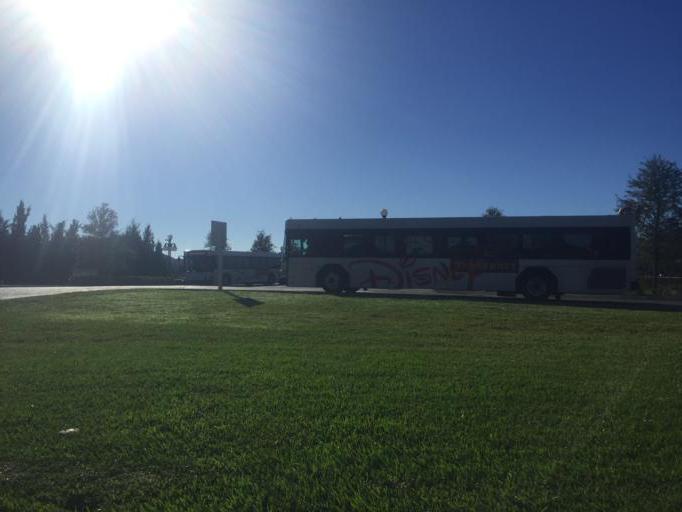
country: US
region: Florida
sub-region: Orange County
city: Bay Hill
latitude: 28.4165
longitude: -81.5778
